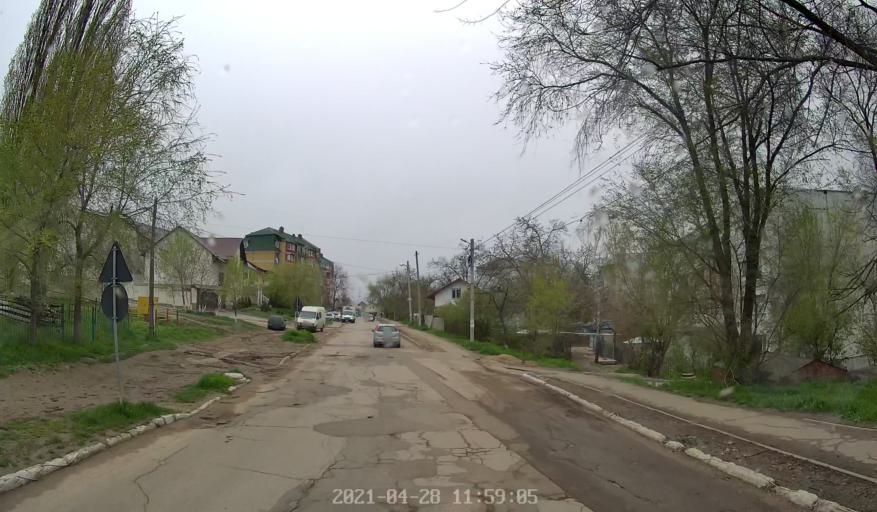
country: MD
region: Chisinau
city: Singera
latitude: 46.9816
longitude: 28.9338
